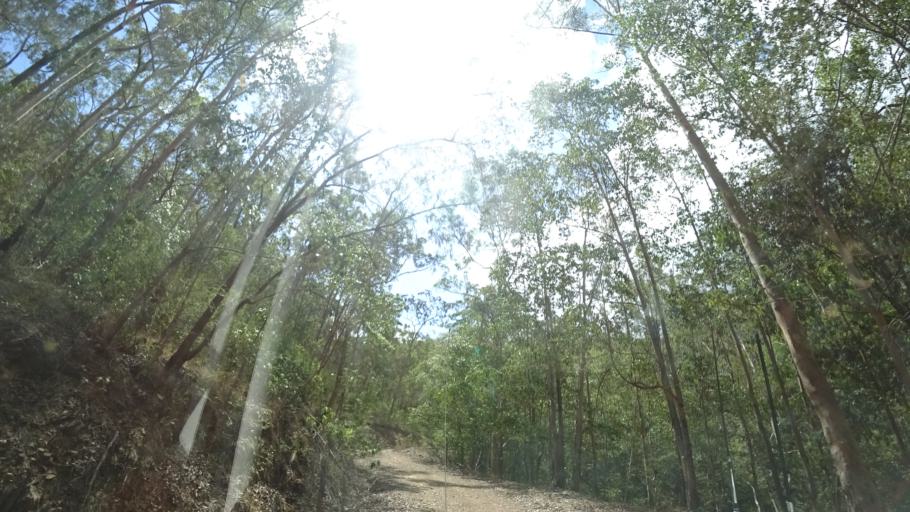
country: AU
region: Queensland
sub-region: Moreton Bay
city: Highvale
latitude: -27.3685
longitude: 152.7342
